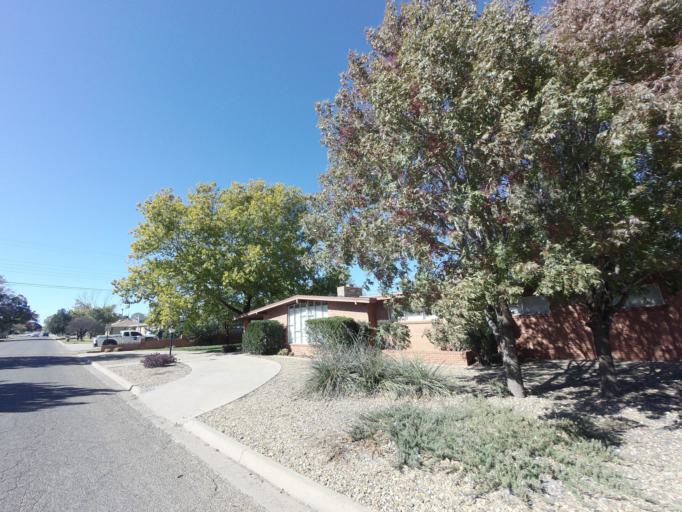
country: US
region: New Mexico
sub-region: Curry County
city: Clovis
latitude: 34.4300
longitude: -103.2005
